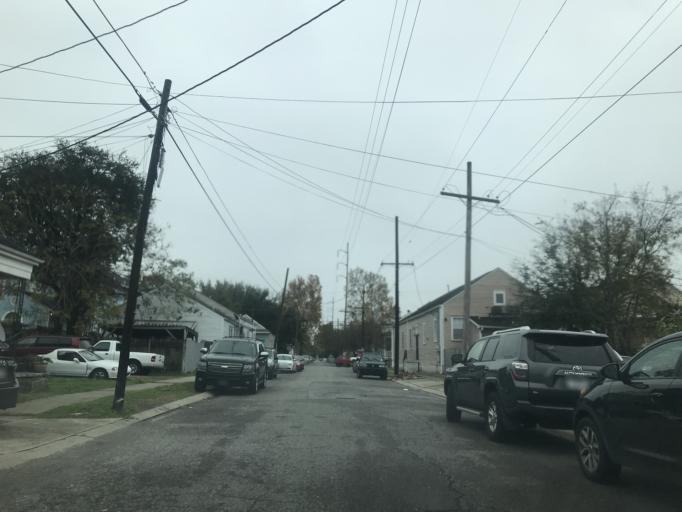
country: US
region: Louisiana
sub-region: Orleans Parish
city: New Orleans
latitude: 29.9707
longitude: -90.1033
